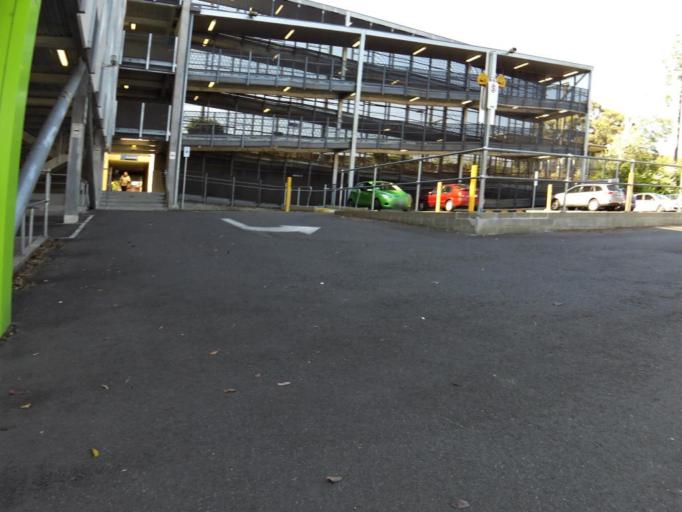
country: AU
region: Victoria
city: Burwood East
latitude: -37.8766
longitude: 145.1491
